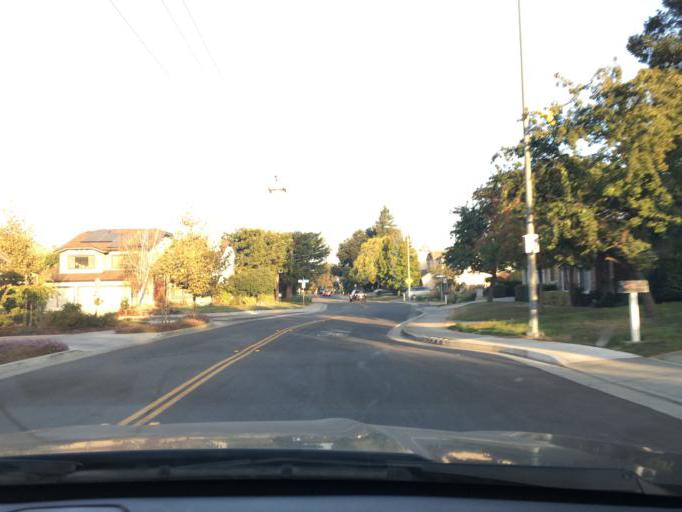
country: US
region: California
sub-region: Santa Clara County
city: Cupertino
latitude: 37.3010
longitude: -122.0453
